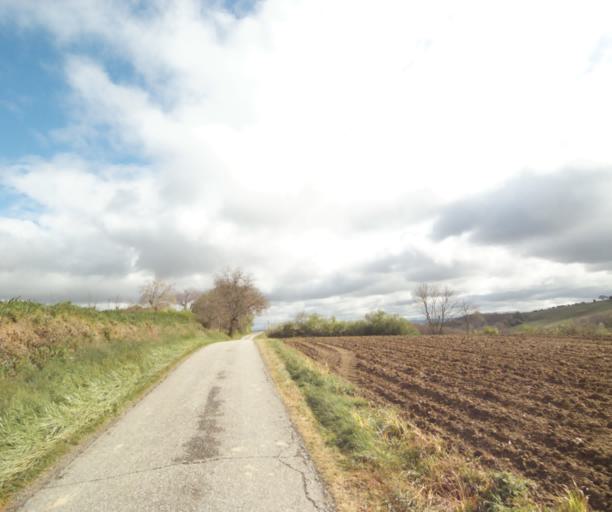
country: FR
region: Midi-Pyrenees
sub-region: Departement de l'Ariege
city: Saverdun
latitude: 43.2035
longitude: 1.5504
